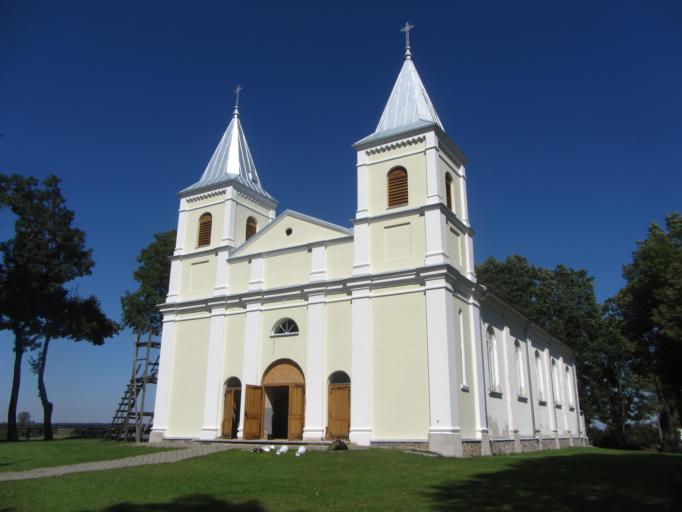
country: LT
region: Alytaus apskritis
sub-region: Alytus
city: Alytus
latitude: 54.4387
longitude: 23.8778
